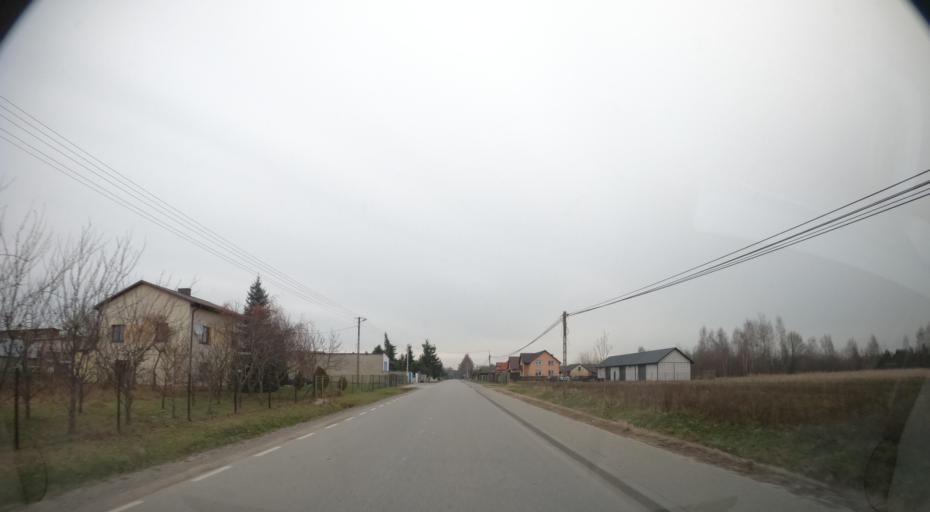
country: PL
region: Masovian Voivodeship
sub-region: Powiat radomski
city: Jedlinsk
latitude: 51.4882
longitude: 21.1329
